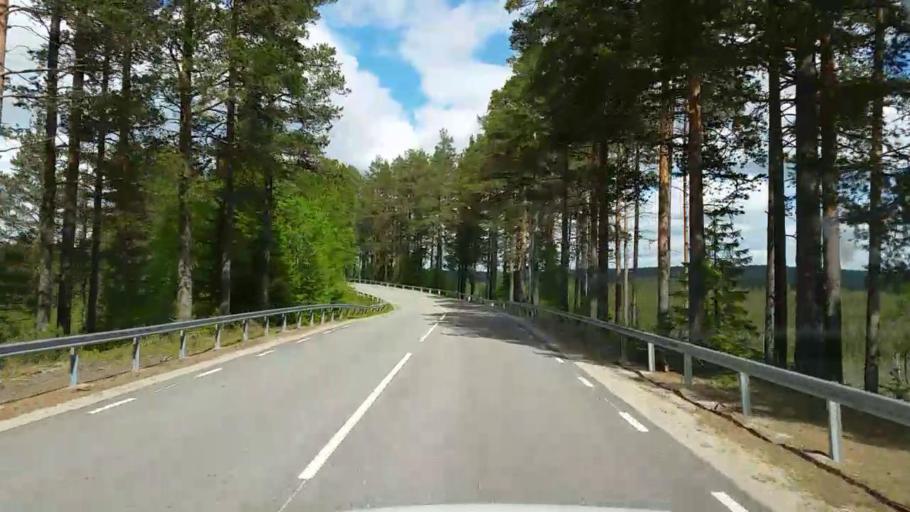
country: SE
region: Gaevleborg
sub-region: Bollnas Kommun
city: Vittsjo
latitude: 61.1241
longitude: 16.1754
